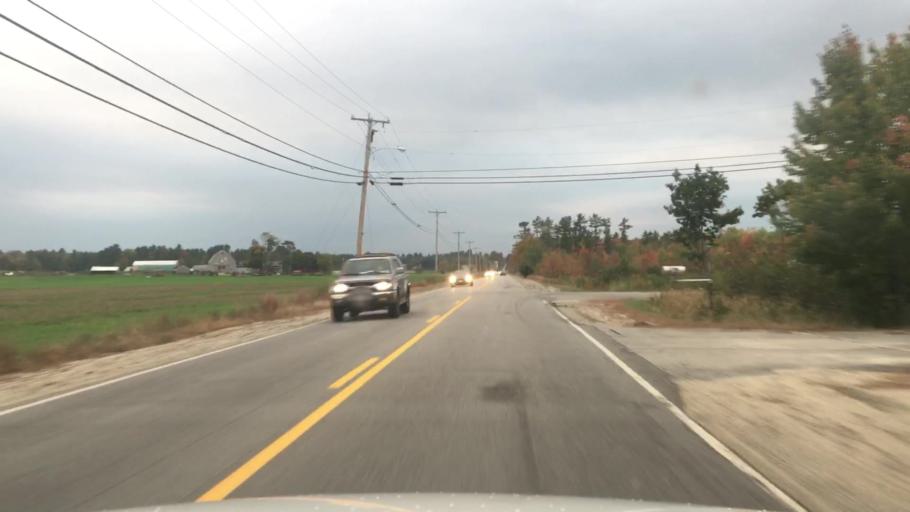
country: US
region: Maine
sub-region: York County
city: Buxton
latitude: 43.6414
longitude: -70.5266
